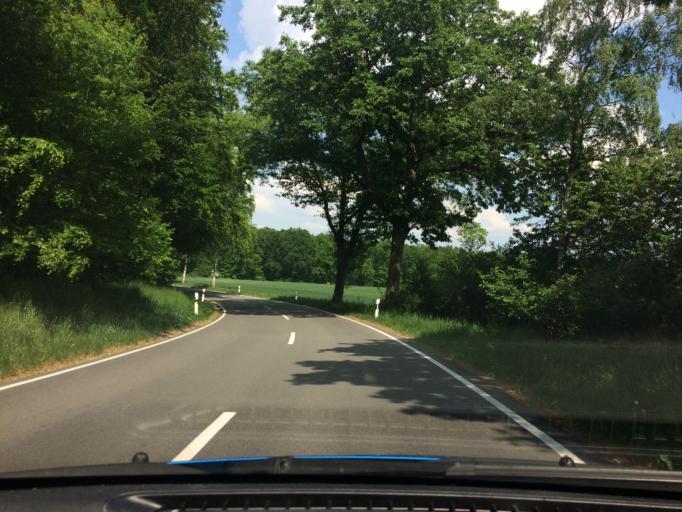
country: DE
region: Lower Saxony
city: Tosterglope
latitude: 53.1997
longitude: 10.8030
